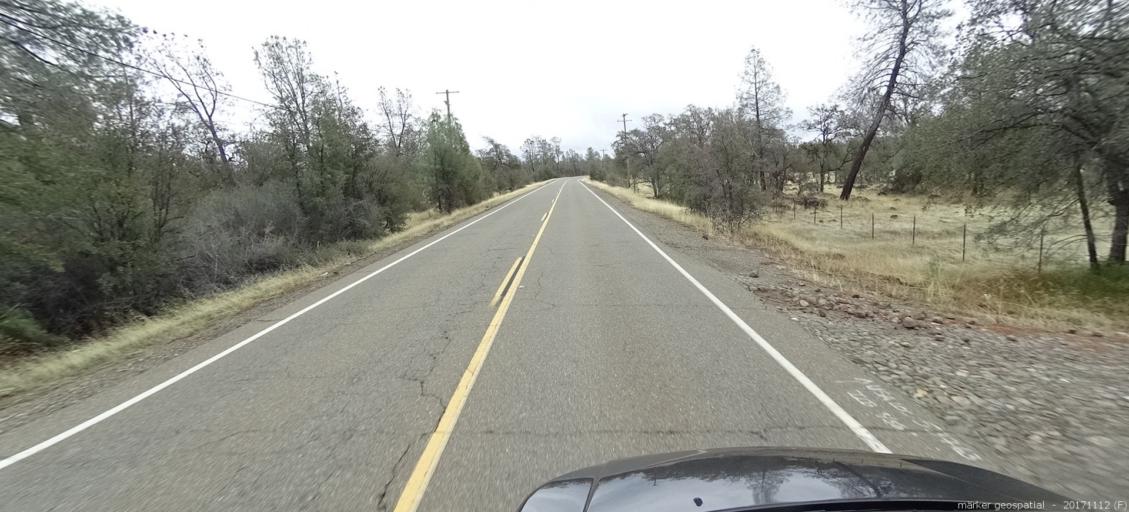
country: US
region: California
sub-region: Shasta County
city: Palo Cedro
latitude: 40.4876
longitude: -122.1235
